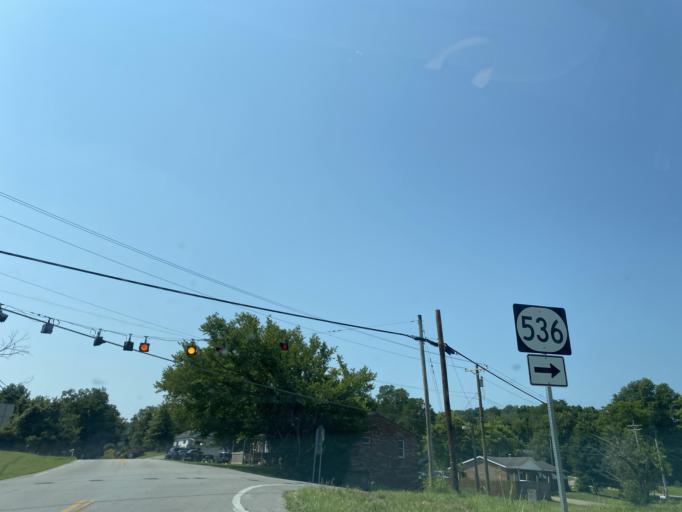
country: US
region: Kentucky
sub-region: Kenton County
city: Ryland Heights
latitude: 38.9132
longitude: -84.4518
